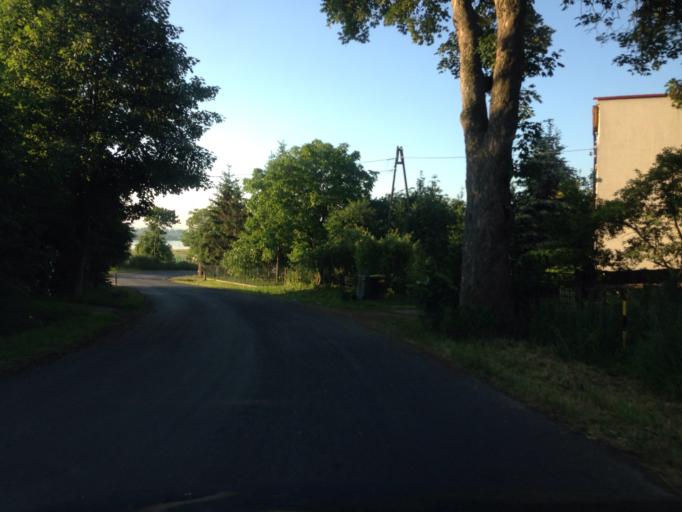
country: PL
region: Pomeranian Voivodeship
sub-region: Powiat tczewski
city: Gniew
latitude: 53.7778
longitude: 18.8309
